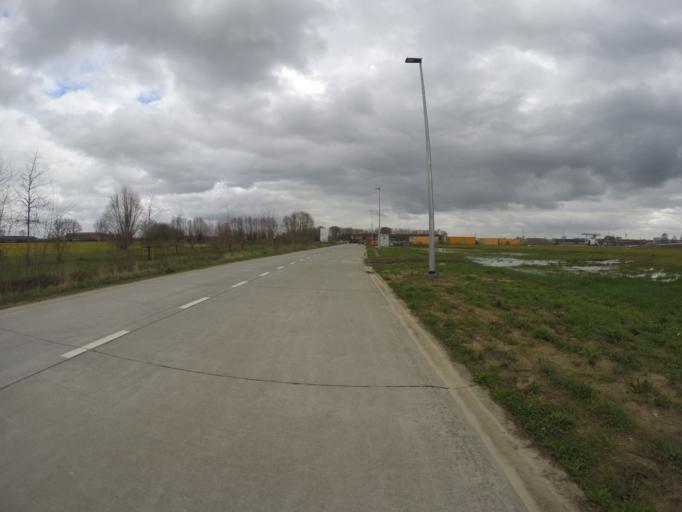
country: BE
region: Flanders
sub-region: Provincie Oost-Vlaanderen
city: Aalter
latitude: 51.1128
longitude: 3.4509
